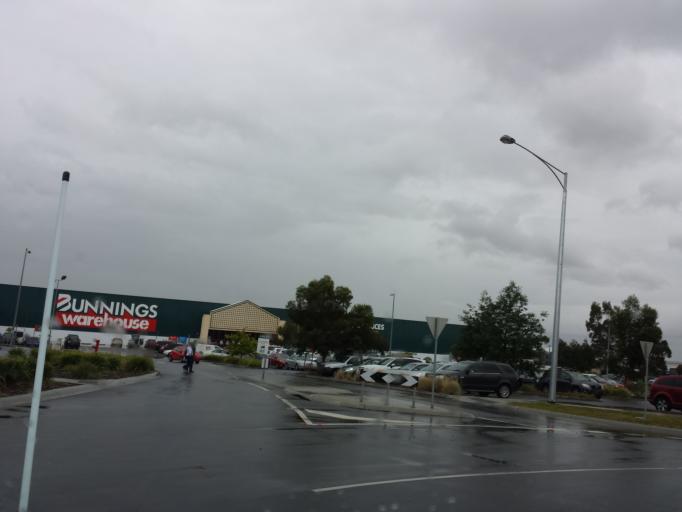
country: AU
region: Victoria
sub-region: Cardinia
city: Officer
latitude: -38.0605
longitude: 145.4557
